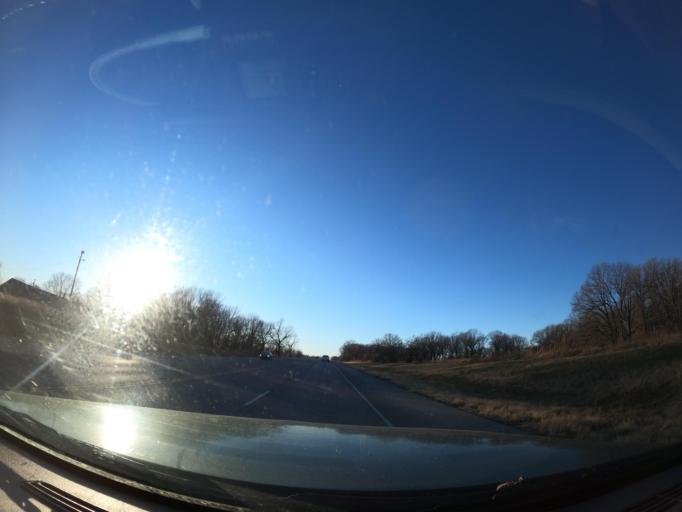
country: US
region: Oklahoma
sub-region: Pittsburg County
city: Hartshorne
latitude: 34.8940
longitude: -95.6317
